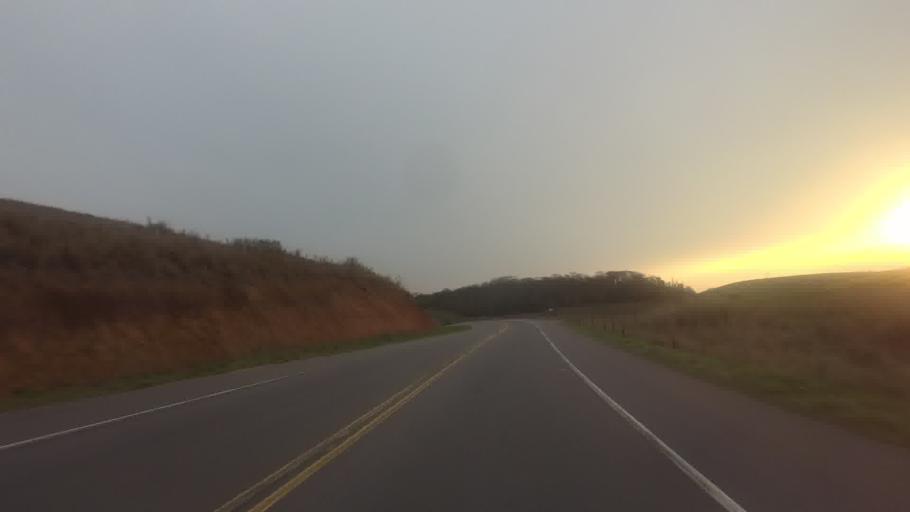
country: BR
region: Minas Gerais
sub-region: Recreio
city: Recreio
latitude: -21.7057
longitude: -42.4227
